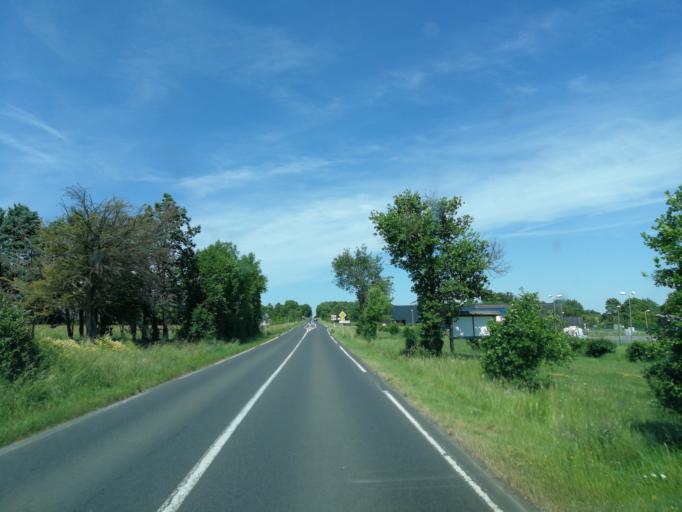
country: FR
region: Poitou-Charentes
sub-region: Departement des Deux-Sevres
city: Saint-Varent
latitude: 46.9039
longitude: -0.2862
